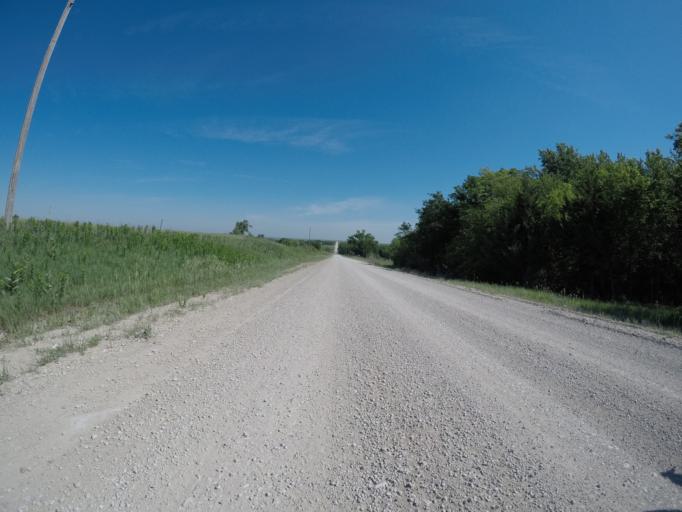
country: US
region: Kansas
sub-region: Wabaunsee County
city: Alma
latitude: 38.9613
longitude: -96.1138
